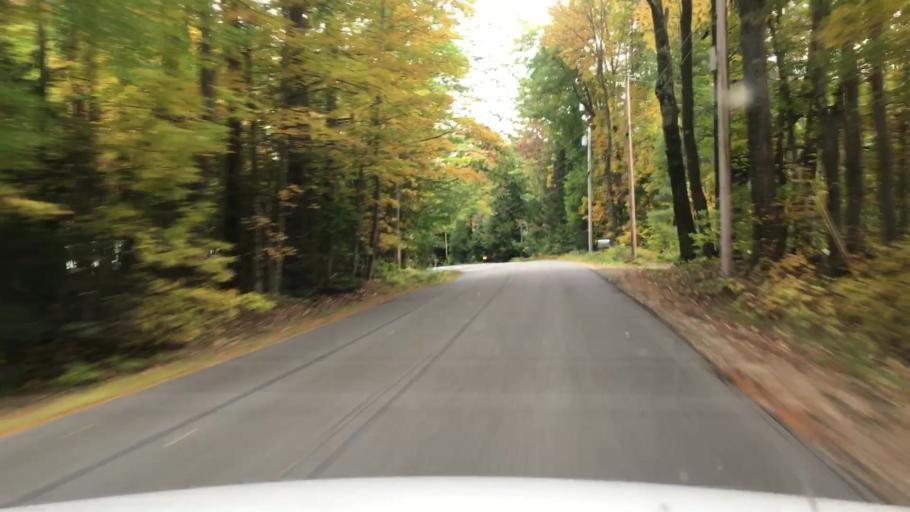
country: US
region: Maine
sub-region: Cumberland County
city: Harrison
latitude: 44.2431
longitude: -70.7189
